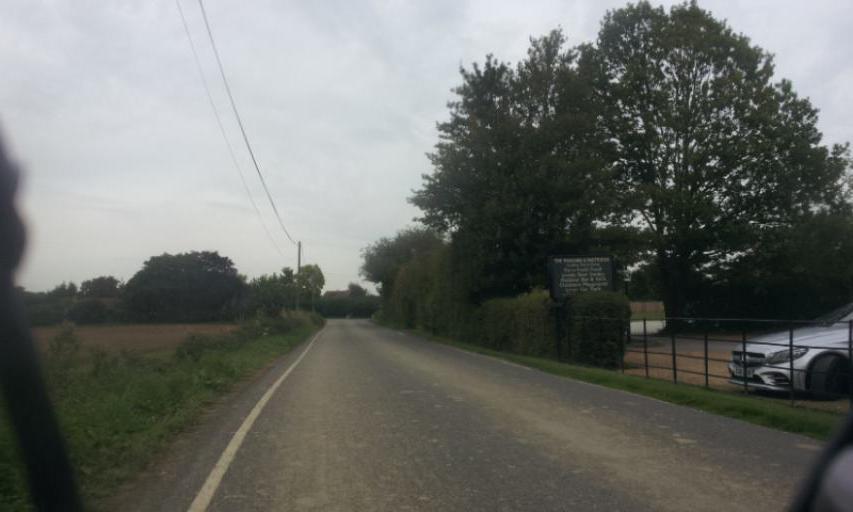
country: GB
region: England
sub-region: Kent
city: Hadlow
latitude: 51.1916
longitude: 0.3201
